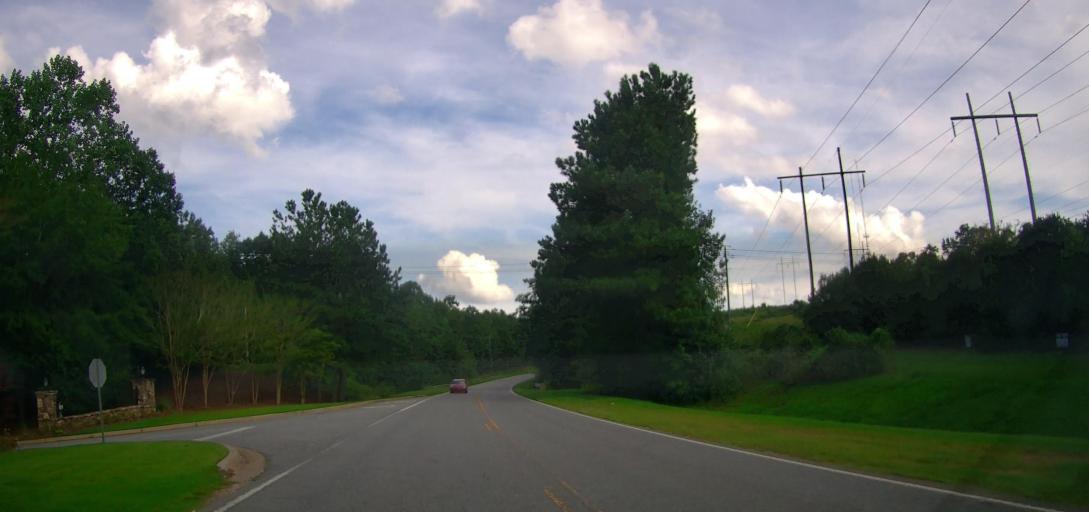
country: US
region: Alabama
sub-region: Russell County
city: Phenix City
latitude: 32.5166
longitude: -85.0136
